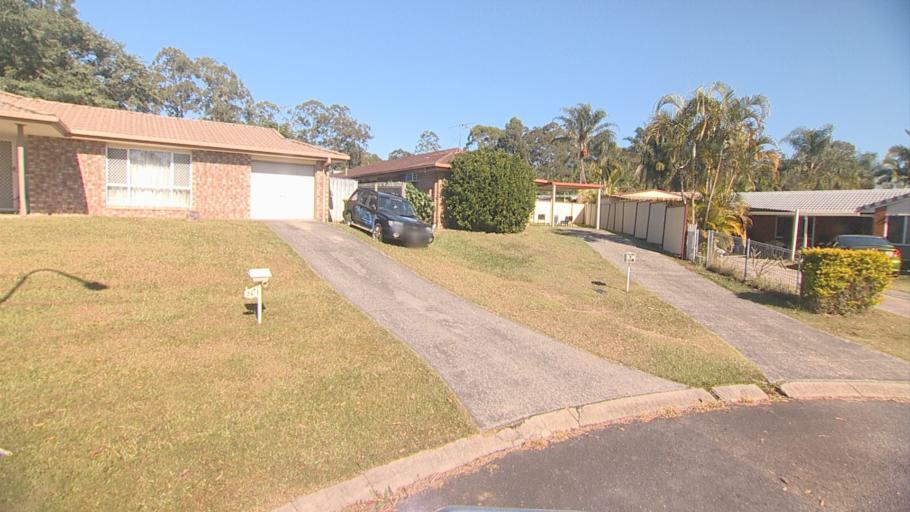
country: AU
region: Queensland
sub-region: Logan
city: Park Ridge South
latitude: -27.6968
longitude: 153.0183
